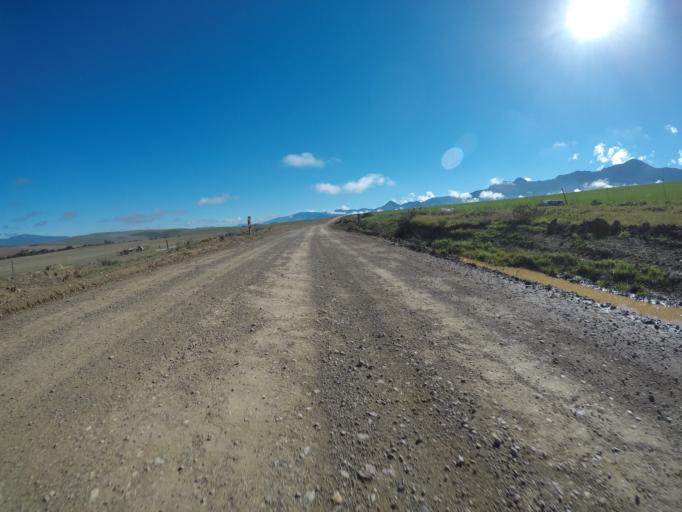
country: ZA
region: Western Cape
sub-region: Overberg District Municipality
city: Caledon
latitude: -34.1182
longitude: 19.7153
